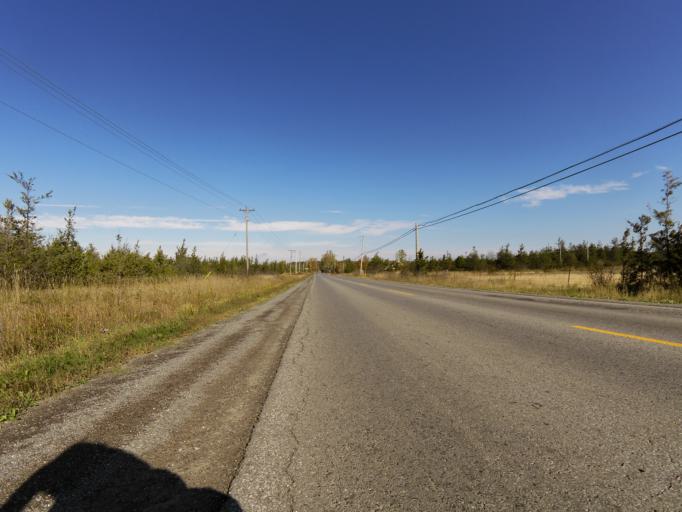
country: CA
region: Ontario
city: Prince Edward
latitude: 44.0218
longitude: -77.3657
